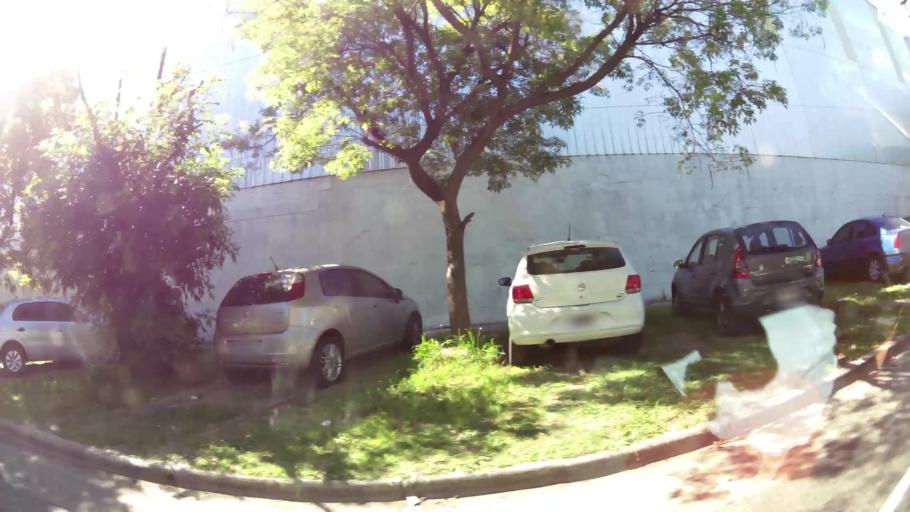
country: AR
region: Buenos Aires
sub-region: Partido de General San Martin
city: General San Martin
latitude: -34.5413
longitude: -58.5268
